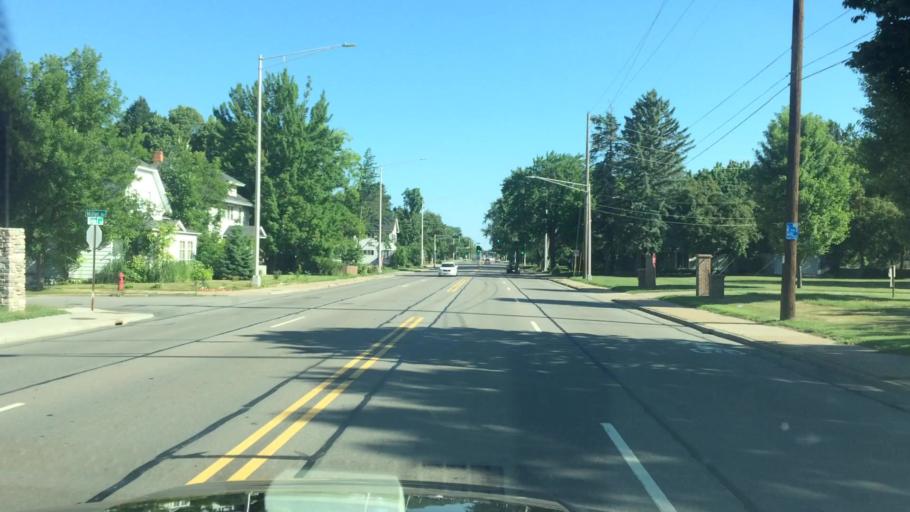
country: US
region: Wisconsin
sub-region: Marathon County
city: Wausau
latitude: 44.9416
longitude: -89.6192
